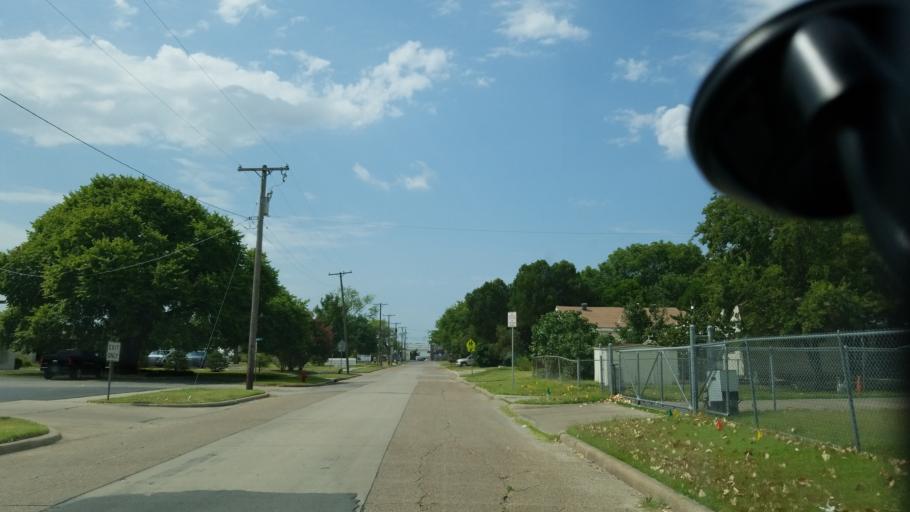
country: US
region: Texas
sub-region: Dallas County
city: Grand Prairie
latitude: 32.7511
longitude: -96.9813
